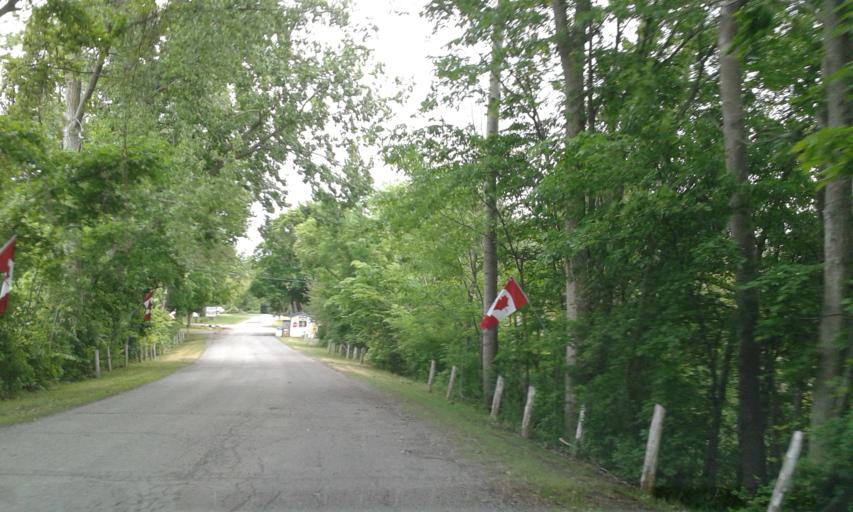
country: CA
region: Ontario
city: Picton
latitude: 44.0631
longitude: -77.0061
